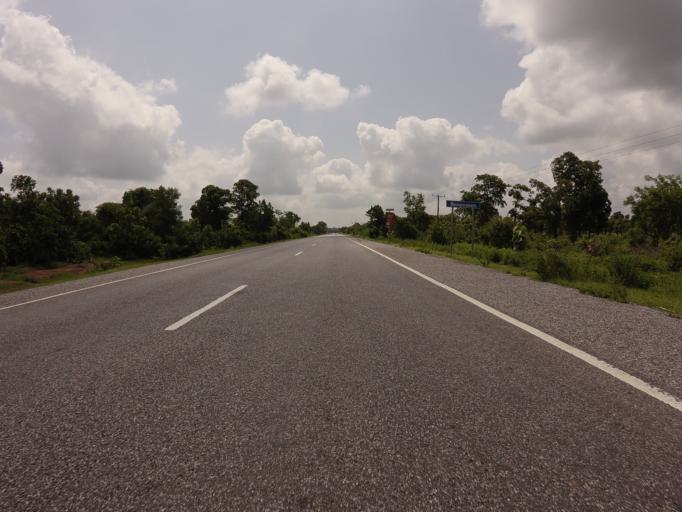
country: GH
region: Northern
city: Tamale
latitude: 9.1293
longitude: -1.6031
